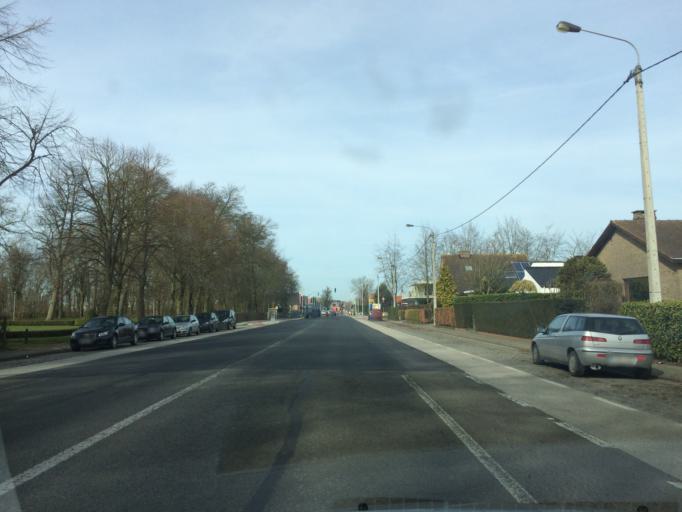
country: BE
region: Flanders
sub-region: Provincie West-Vlaanderen
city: Diksmuide
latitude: 51.0212
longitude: 2.8655
